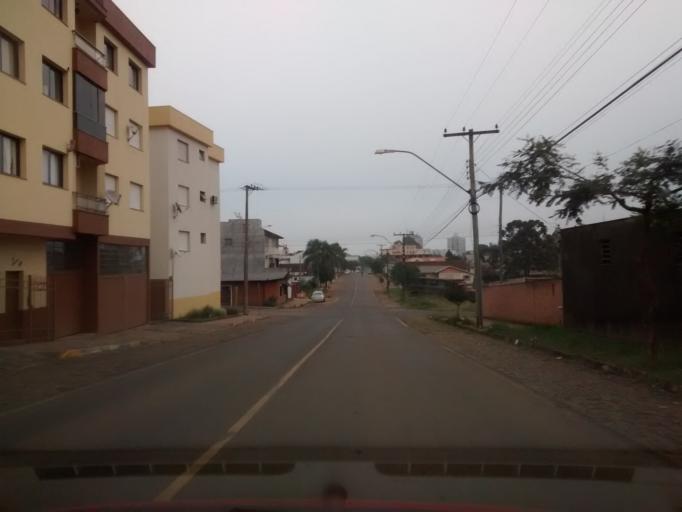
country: BR
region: Rio Grande do Sul
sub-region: Vacaria
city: Vacaria
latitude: -28.5042
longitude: -50.9259
